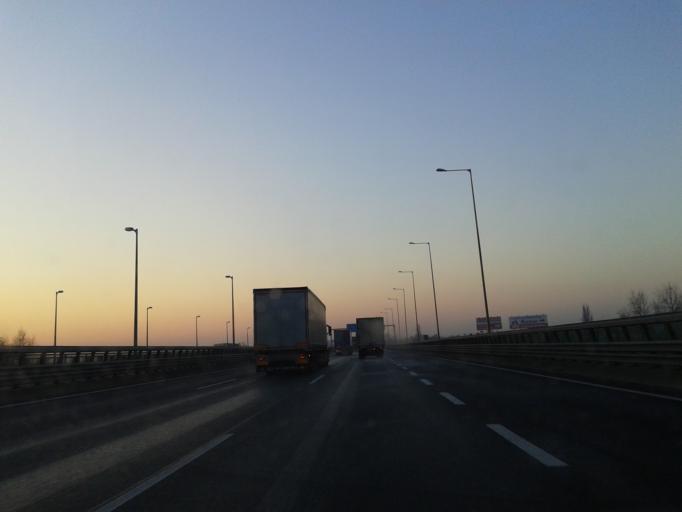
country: HU
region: Pest
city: Halasztelek
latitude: 47.3874
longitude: 19.0142
